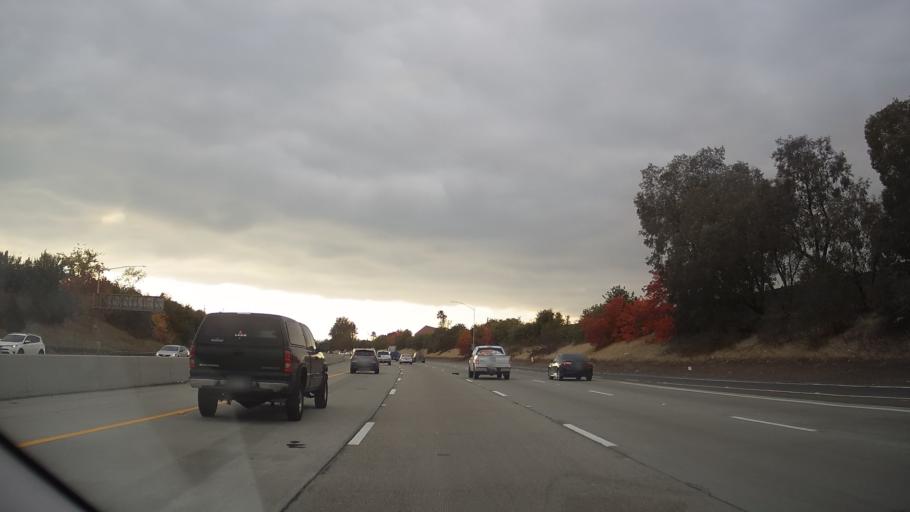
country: US
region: California
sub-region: Sacramento County
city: Rio Linda
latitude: 38.6434
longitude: -121.4325
